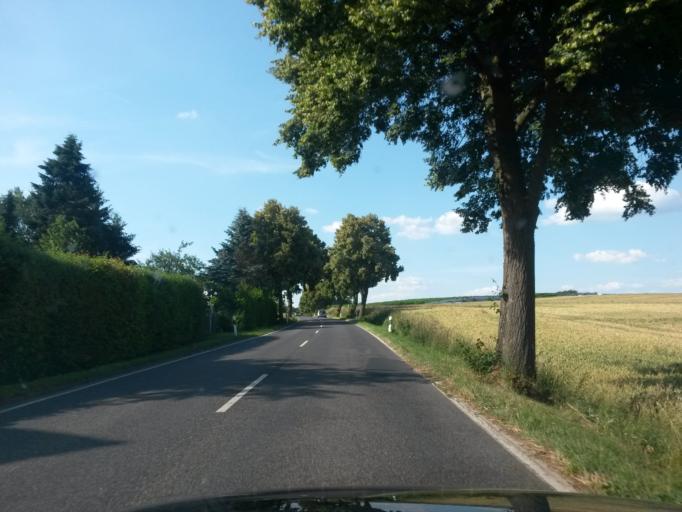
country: DE
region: North Rhine-Westphalia
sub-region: Regierungsbezirk Koln
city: Much
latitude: 50.8914
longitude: 7.3421
